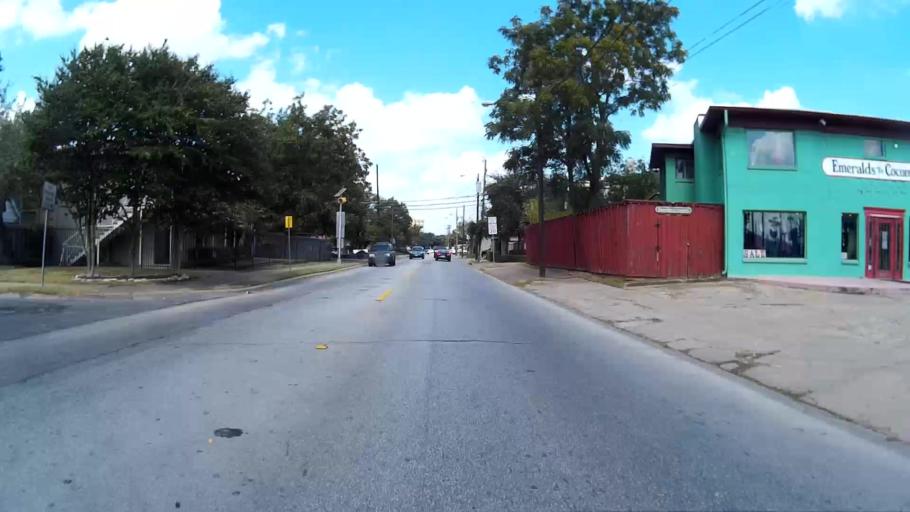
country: US
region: Texas
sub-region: Dallas County
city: Highland Park
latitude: 32.8183
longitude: -96.7825
